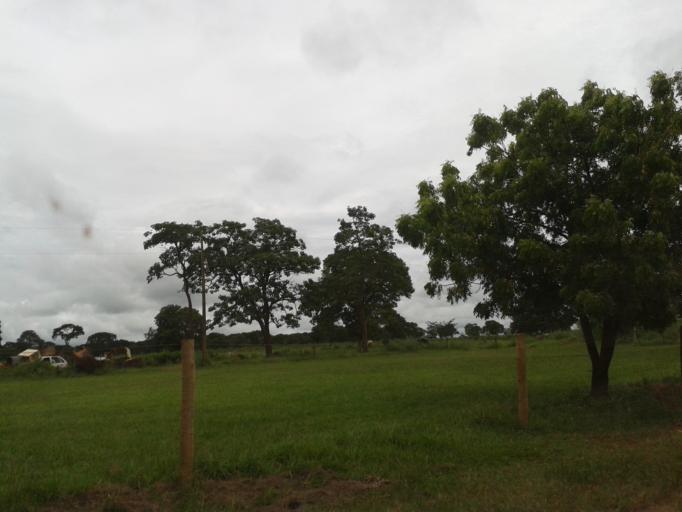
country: BR
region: Minas Gerais
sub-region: Capinopolis
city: Capinopolis
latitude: -18.7972
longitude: -49.7876
